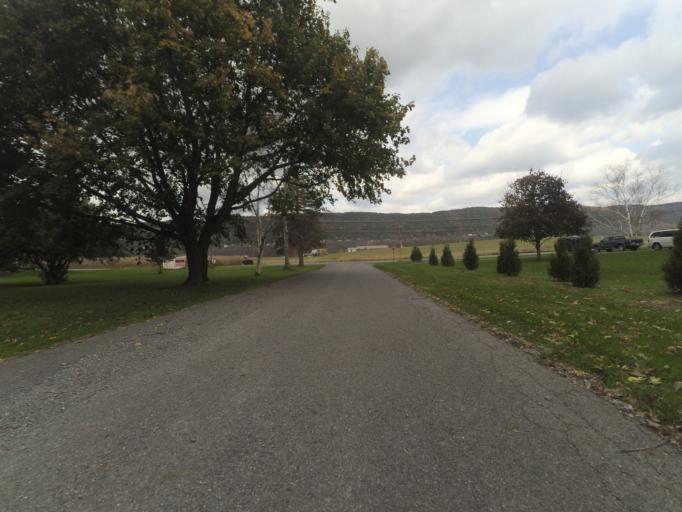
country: US
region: Pennsylvania
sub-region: Centre County
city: Bellefonte
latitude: 40.8914
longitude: -77.8156
